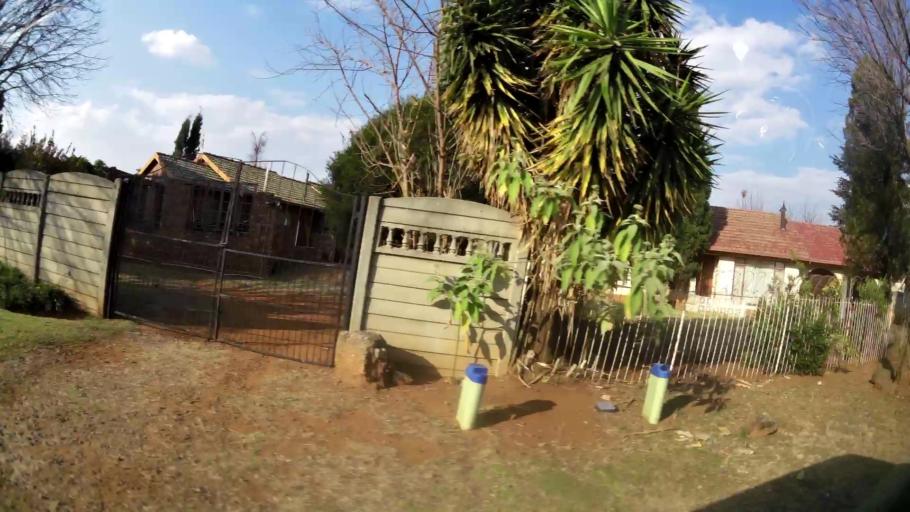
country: ZA
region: Gauteng
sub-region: Ekurhuleni Metropolitan Municipality
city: Benoni
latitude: -26.1276
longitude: 28.3693
